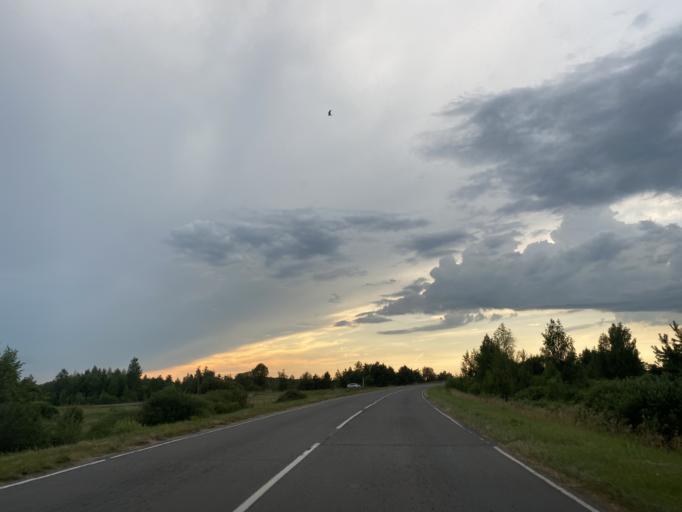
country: BY
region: Brest
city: Ivanava
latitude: 52.3810
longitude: 25.5736
